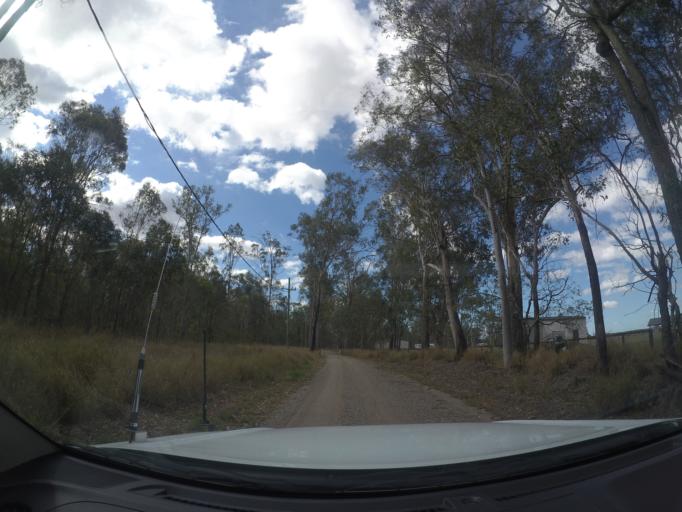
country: AU
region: Queensland
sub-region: Logan
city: North Maclean
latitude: -27.8090
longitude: 152.9932
